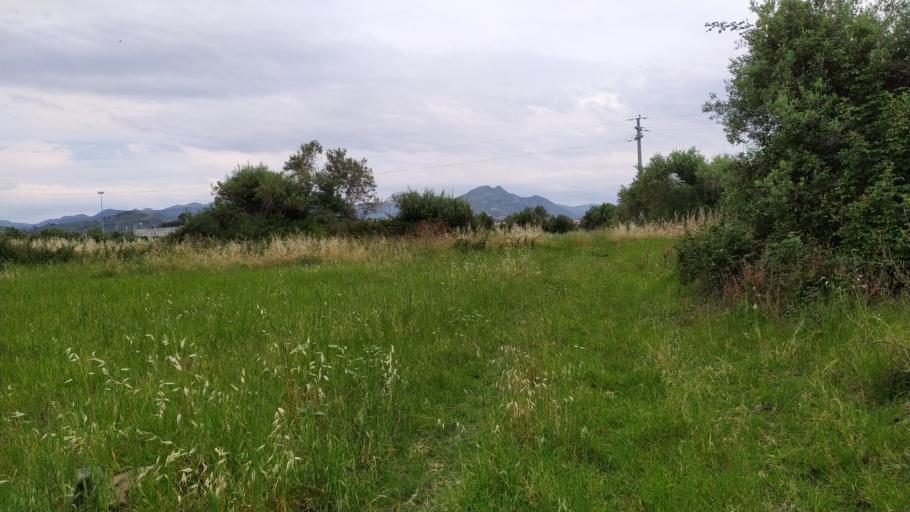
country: IT
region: Sicily
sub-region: Messina
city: San Filippo del Mela
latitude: 38.1839
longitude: 15.2629
